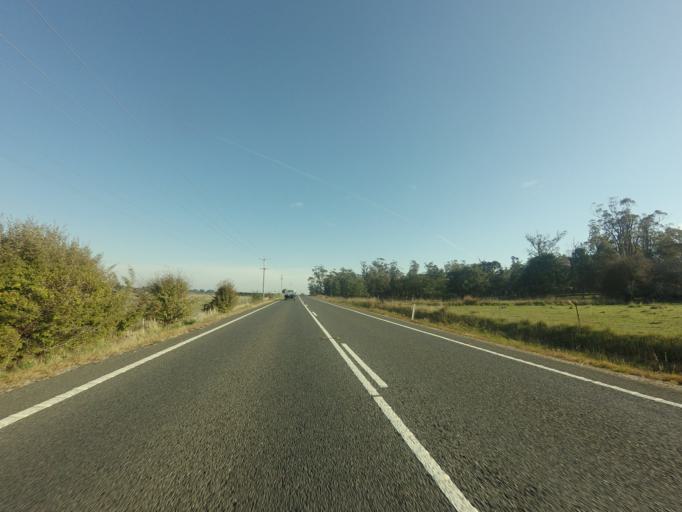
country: AU
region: Tasmania
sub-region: Northern Midlands
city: Longford
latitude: -41.5649
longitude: 147.0795
